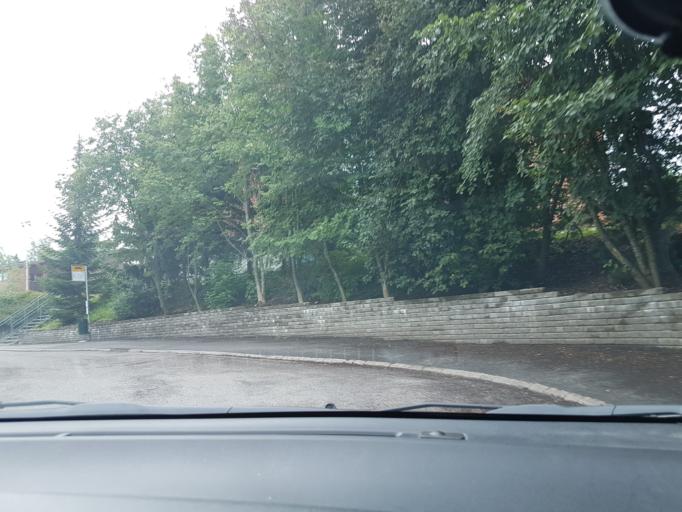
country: FI
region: Uusimaa
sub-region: Helsinki
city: Vantaa
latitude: 60.2658
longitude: 25.0155
